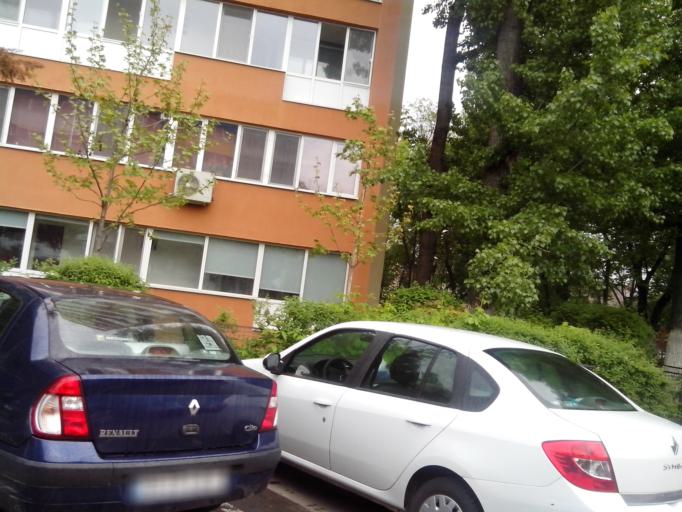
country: RO
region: Bucuresti
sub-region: Municipiul Bucuresti
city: Bucuresti
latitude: 44.4226
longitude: 26.1044
